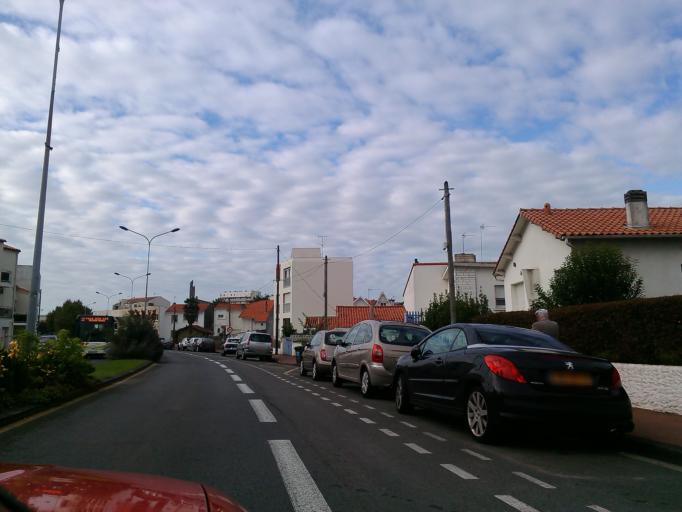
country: FR
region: Poitou-Charentes
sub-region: Departement de la Charente-Maritime
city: Royan
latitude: 45.6300
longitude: -1.0327
